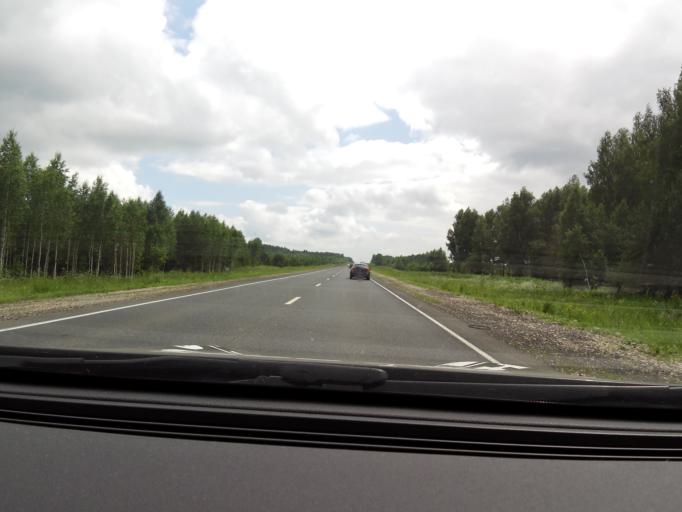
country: RU
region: Perm
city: Orda
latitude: 57.2340
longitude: 57.0652
